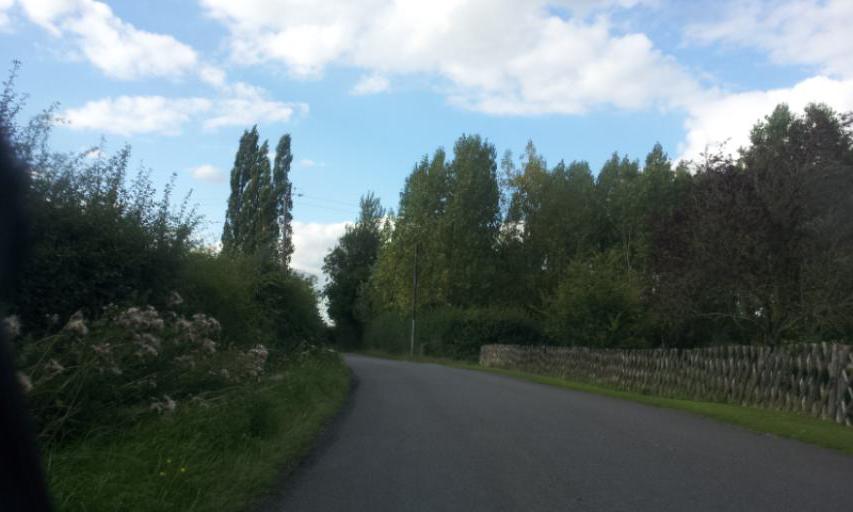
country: GB
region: England
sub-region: Kent
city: Headcorn
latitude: 51.1782
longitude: 0.6249
